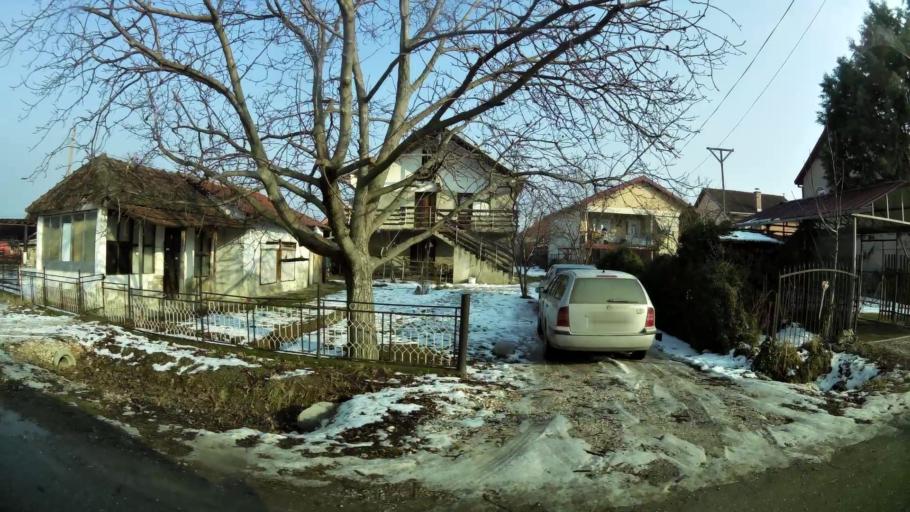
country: MK
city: Kadino
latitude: 41.9686
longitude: 21.6006
